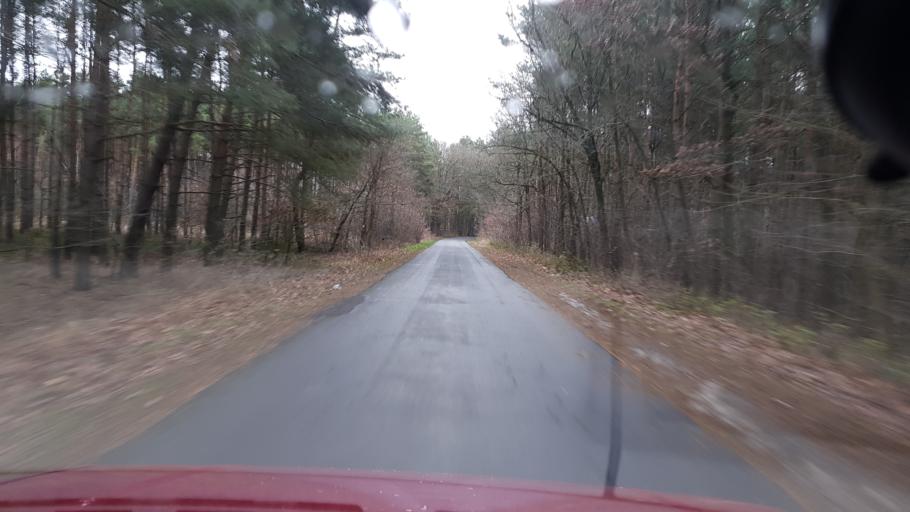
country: PL
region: West Pomeranian Voivodeship
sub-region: Powiat stargardzki
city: Stargard Szczecinski
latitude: 53.3269
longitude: 15.1113
